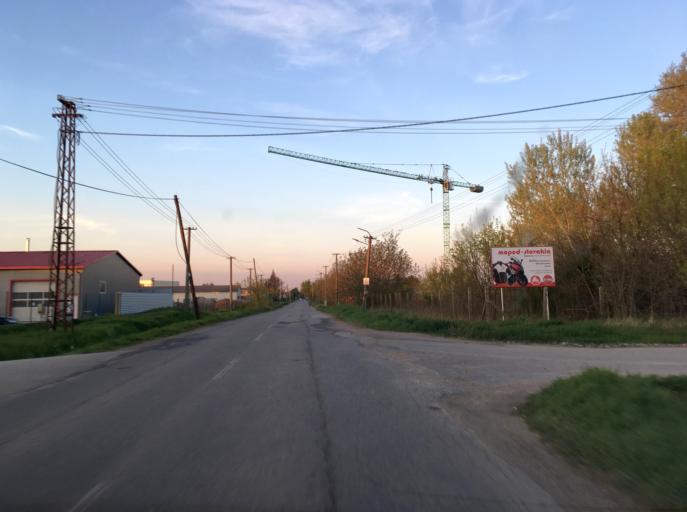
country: SK
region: Nitriansky
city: Kolarovo
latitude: 47.9060
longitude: 17.9787
